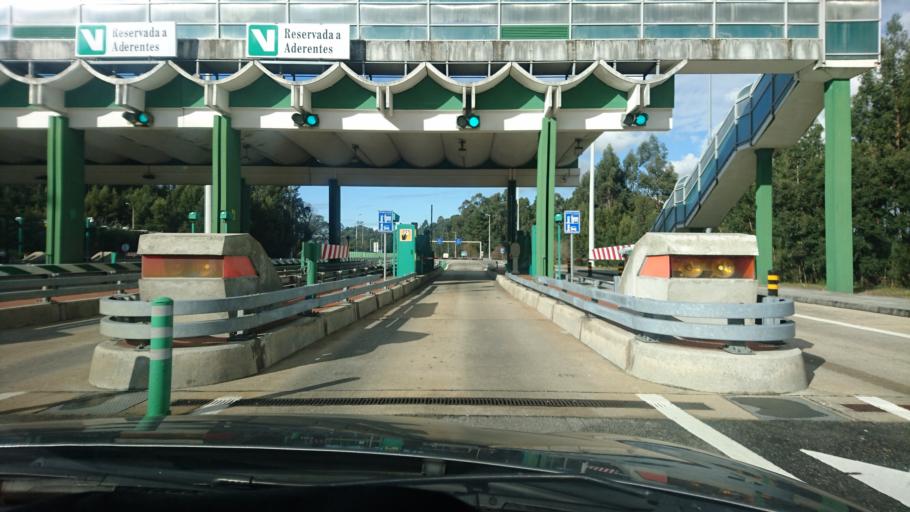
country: PT
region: Aveiro
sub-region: Santa Maria da Feira
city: Feira
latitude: 40.9274
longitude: -8.5649
